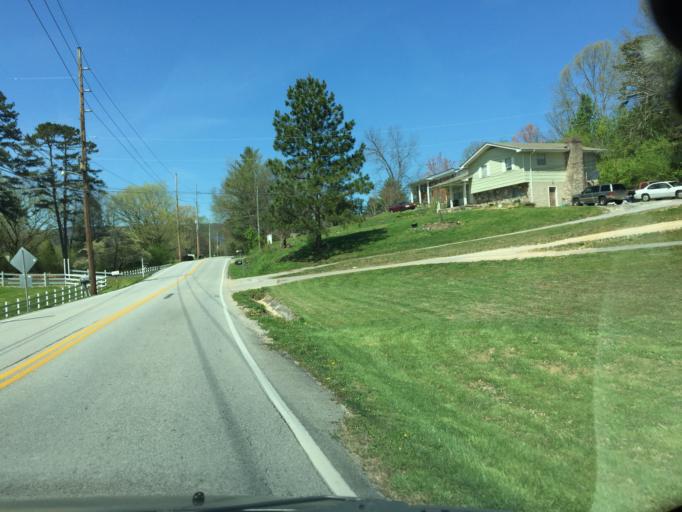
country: US
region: Tennessee
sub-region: Hamilton County
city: Middle Valley
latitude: 35.1988
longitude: -85.2019
